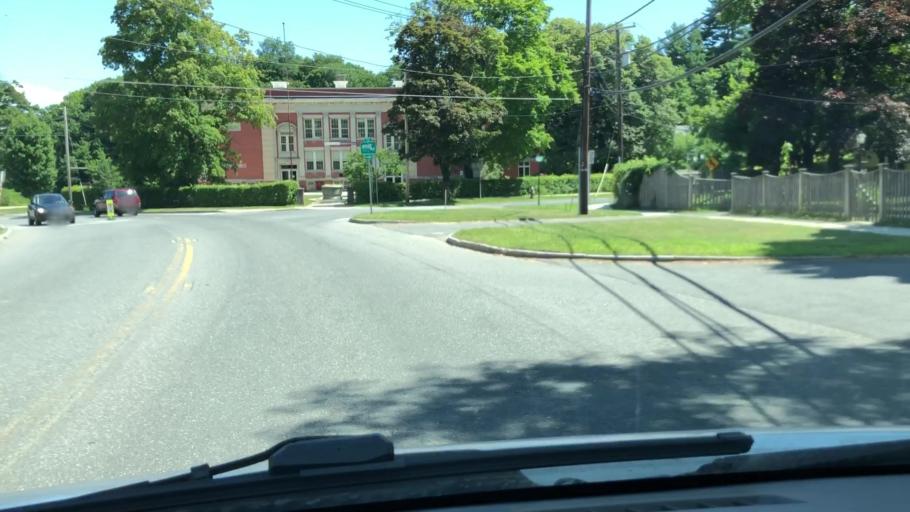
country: US
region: Massachusetts
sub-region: Hampshire County
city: Williamsburg
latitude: 42.3917
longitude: -72.7294
